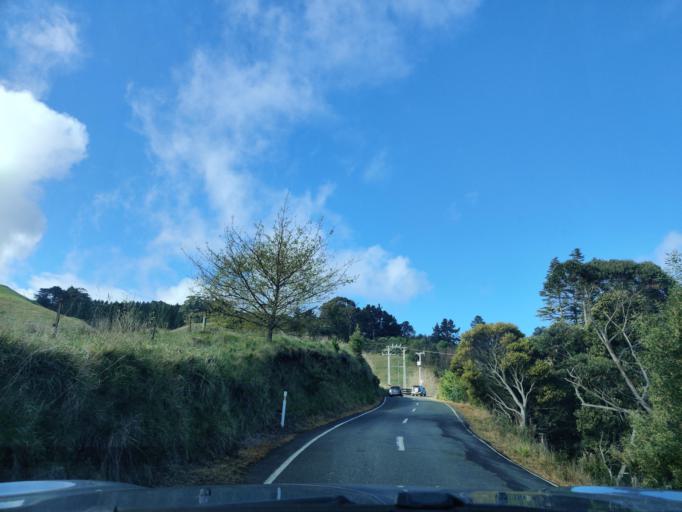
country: NZ
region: Hawke's Bay
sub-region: Hastings District
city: Hastings
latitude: -39.6929
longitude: 176.9018
